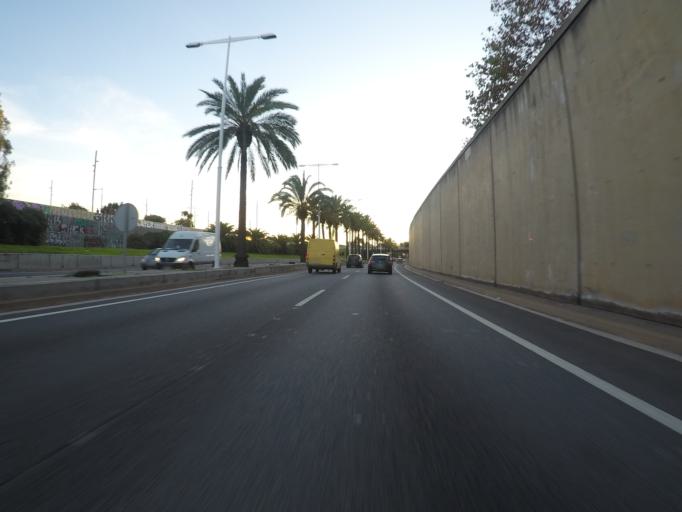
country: ES
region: Catalonia
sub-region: Provincia de Barcelona
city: Sant Adria de Besos
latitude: 41.4080
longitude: 2.2202
